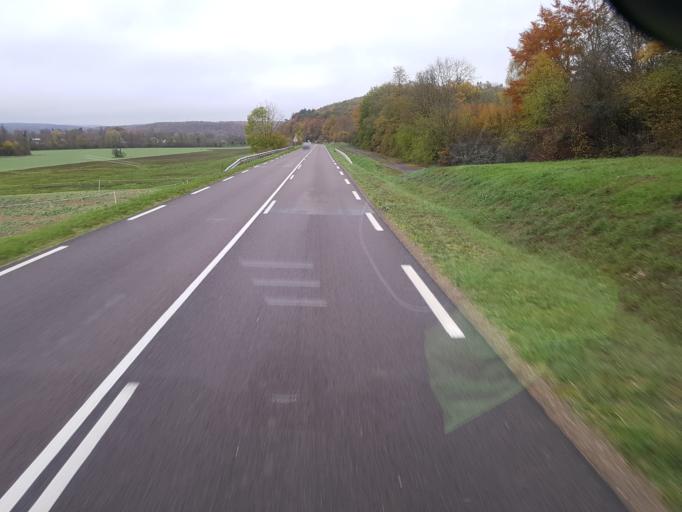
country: FR
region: Bourgogne
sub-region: Departement de la Cote-d'Or
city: Is-sur-Tille
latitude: 47.5284
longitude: 4.9950
